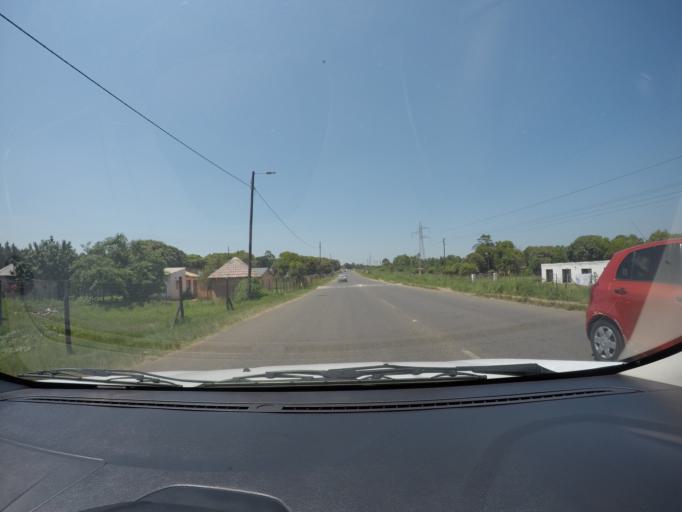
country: ZA
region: KwaZulu-Natal
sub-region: uThungulu District Municipality
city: eSikhawini
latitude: -28.8298
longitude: 31.9421
